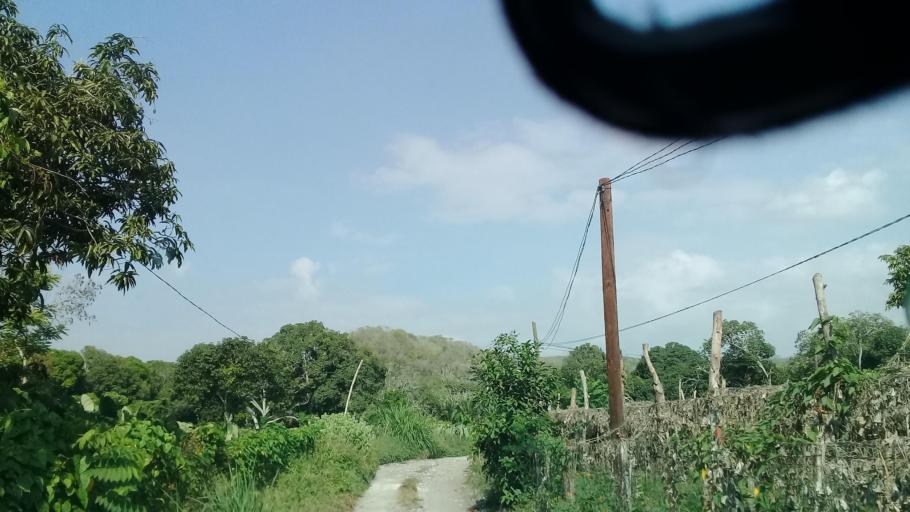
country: MX
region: Veracruz
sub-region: Emiliano Zapata
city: Plan del Rio
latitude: 19.4226
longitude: -96.6146
